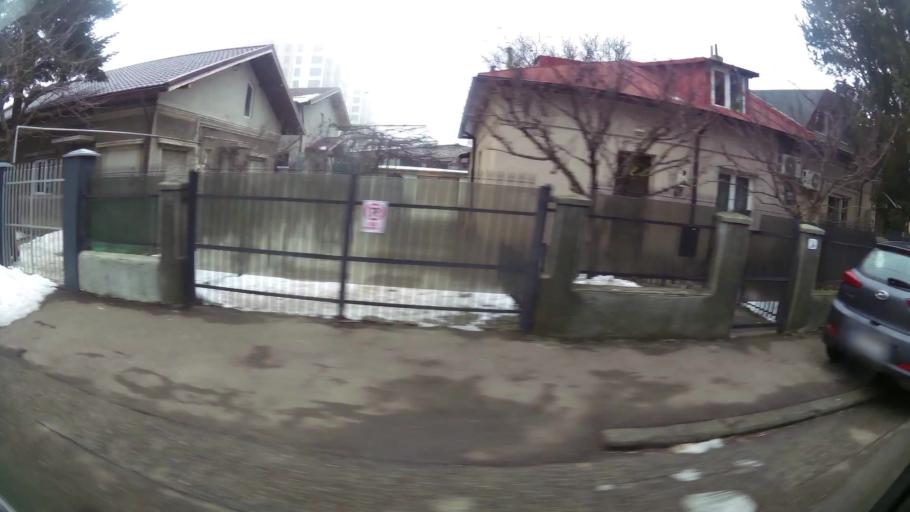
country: RO
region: Ilfov
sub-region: Comuna Chiajna
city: Rosu
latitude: 44.4430
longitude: 26.0242
